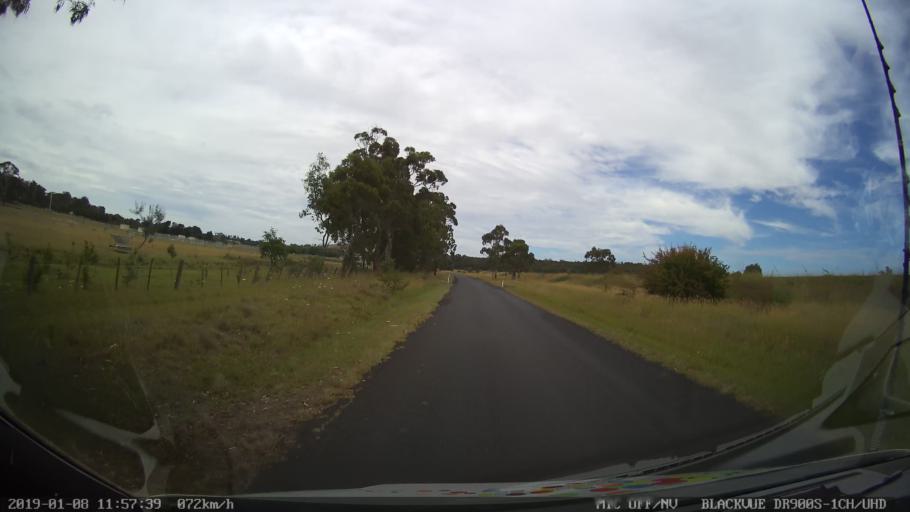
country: AU
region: New South Wales
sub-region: Armidale Dumaresq
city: Armidale
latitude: -30.4519
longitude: 151.5684
